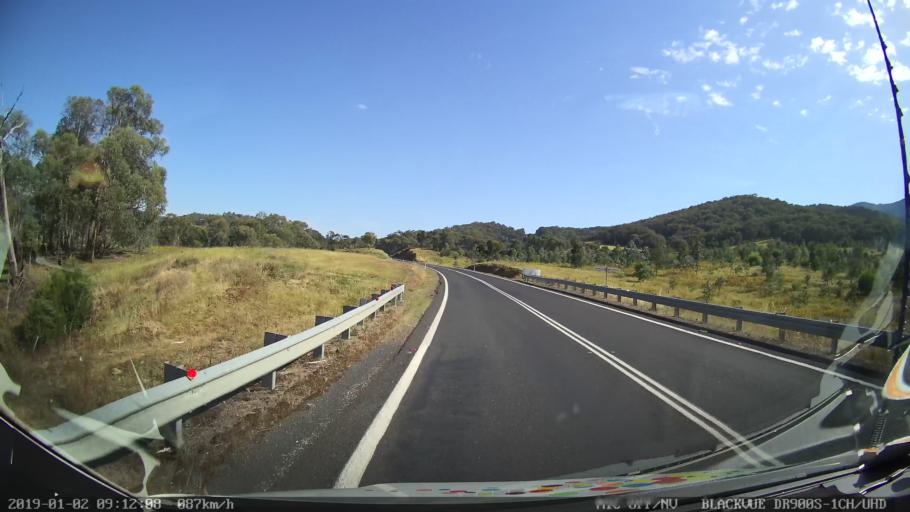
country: AU
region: New South Wales
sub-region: Tumut Shire
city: Tumut
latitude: -35.5041
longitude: 148.2726
